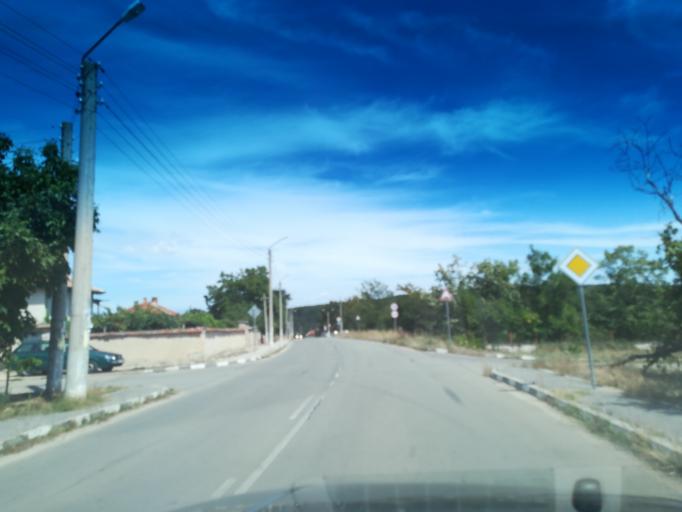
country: BG
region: Plovdiv
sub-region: Obshtina Suedinenie
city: Suedinenie
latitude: 42.4249
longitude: 24.5317
